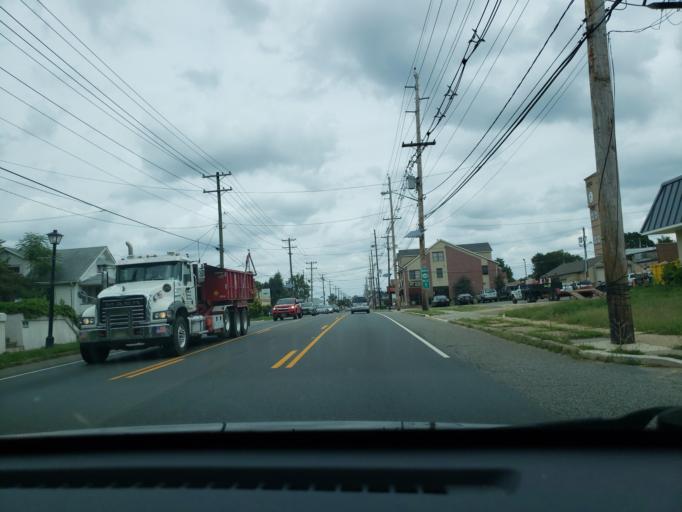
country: US
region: New Jersey
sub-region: Camden County
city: Glendora
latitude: 39.8388
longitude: -75.0689
